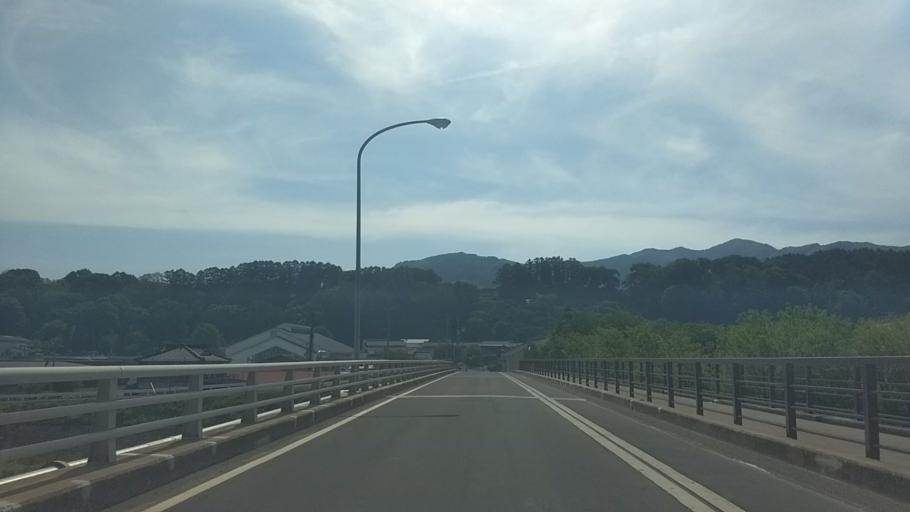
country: JP
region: Nagano
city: Saku
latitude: 36.1372
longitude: 138.4735
